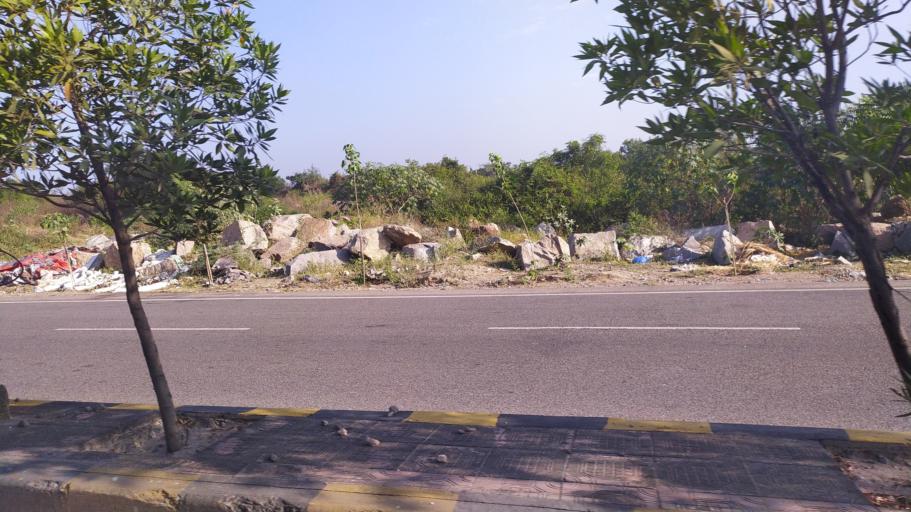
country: IN
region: Telangana
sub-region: Hyderabad
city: Hyderabad
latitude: 17.3206
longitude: 78.3870
